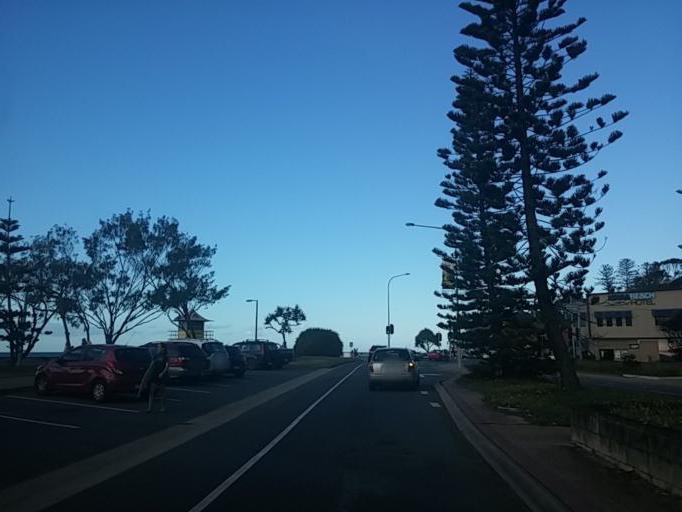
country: AU
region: New South Wales
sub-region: Tweed
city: Tweed Heads West
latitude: -28.1676
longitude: 153.5303
